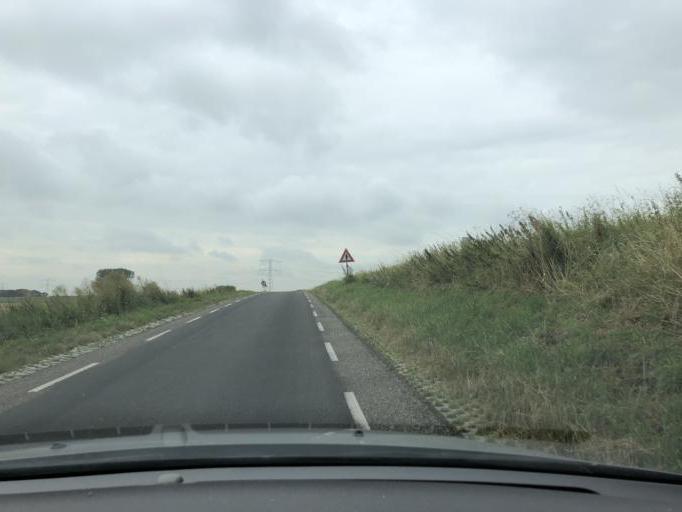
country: NL
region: Zeeland
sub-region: Gemeente Reimerswaal
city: Yerseke
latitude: 51.4666
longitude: 4.0490
